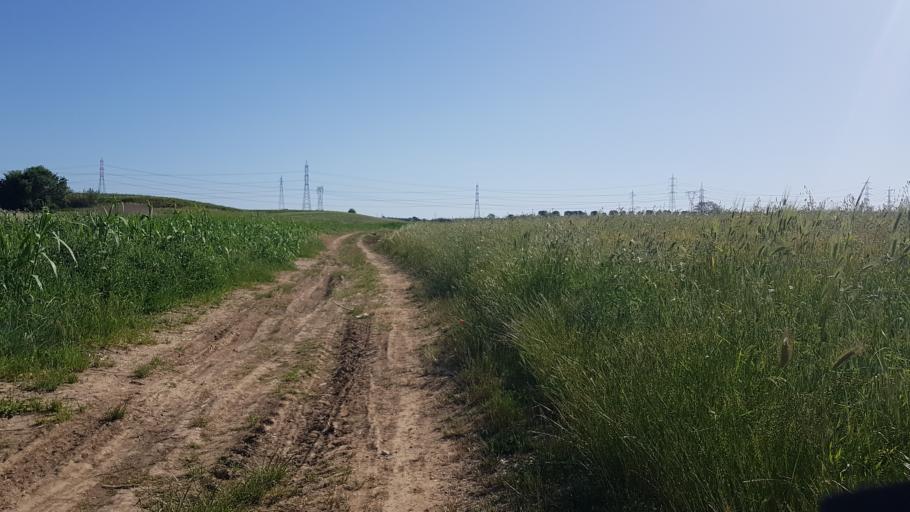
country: IT
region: Apulia
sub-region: Provincia di Brindisi
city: La Rosa
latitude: 40.6033
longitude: 17.9319
